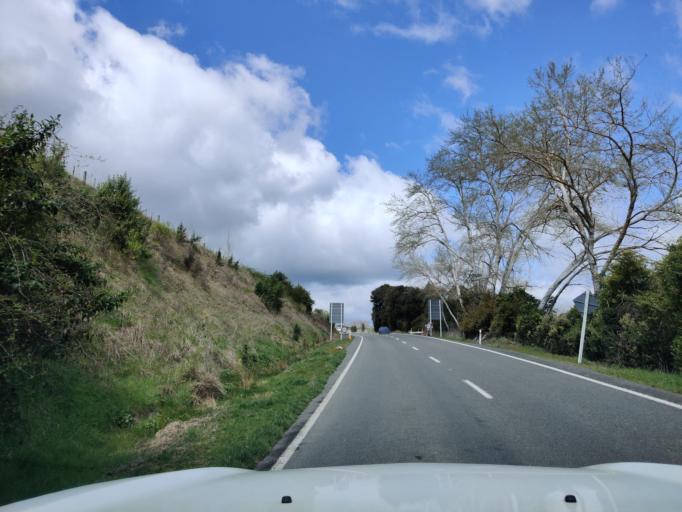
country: NZ
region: Manawatu-Wanganui
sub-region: Ruapehu District
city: Waiouru
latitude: -39.6485
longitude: 175.3244
